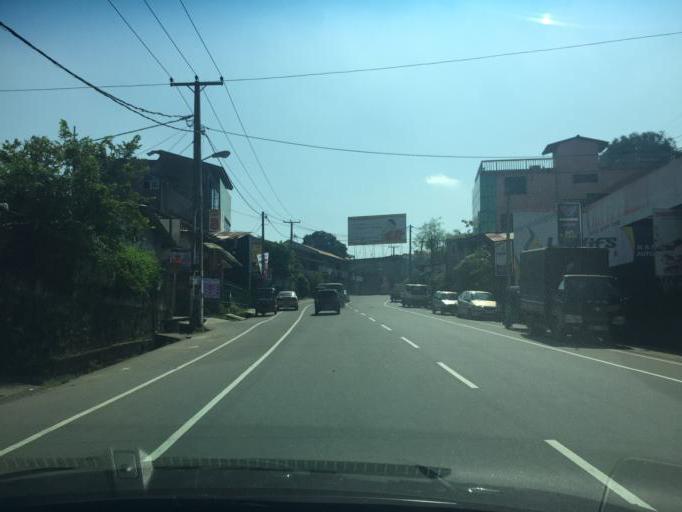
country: LK
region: Western
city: Sri Jayewardenepura Kotte
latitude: 6.8574
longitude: 79.8933
